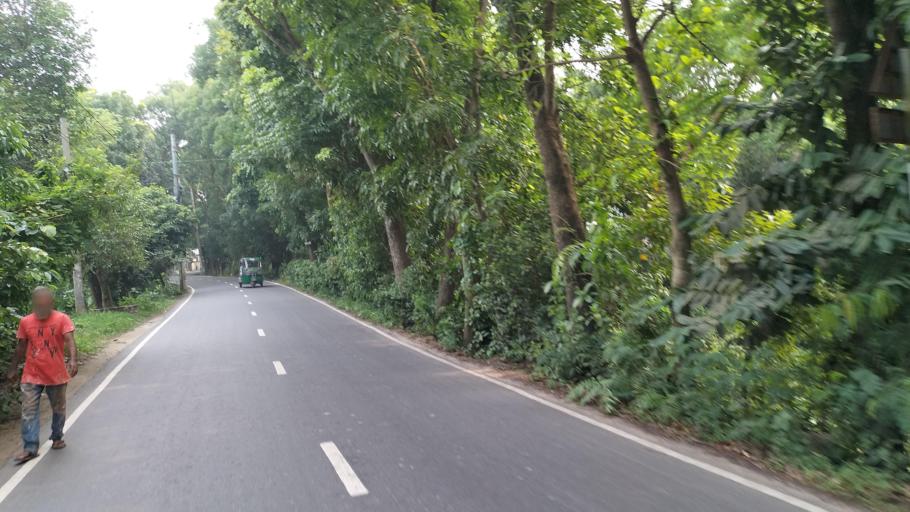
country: BD
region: Dhaka
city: Azimpur
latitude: 23.7000
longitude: 90.2943
